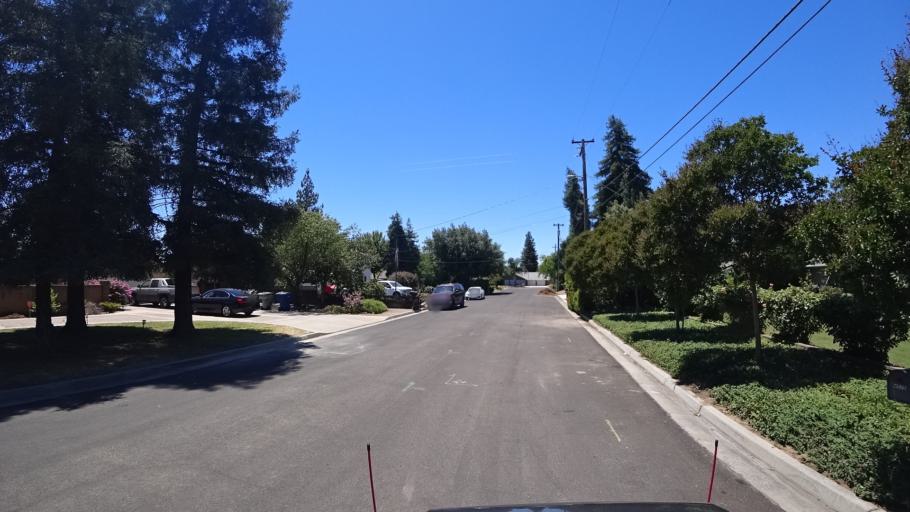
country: US
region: California
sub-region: Fresno County
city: Tarpey Village
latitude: 36.8022
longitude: -119.7463
